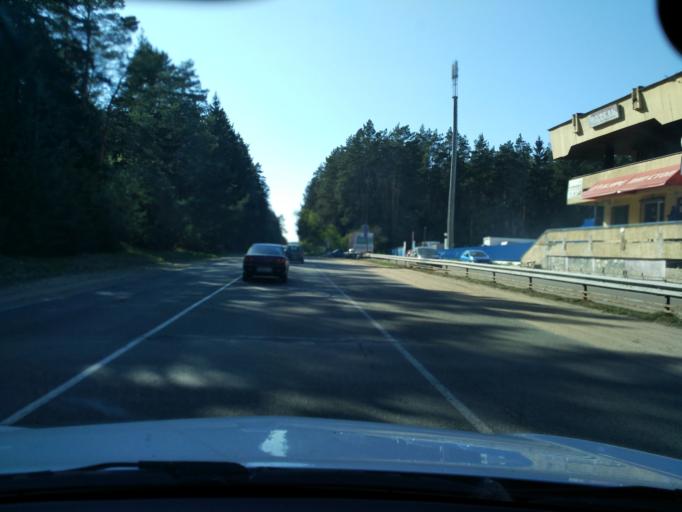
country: BY
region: Minsk
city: Borovlyany
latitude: 53.9623
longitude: 27.6841
